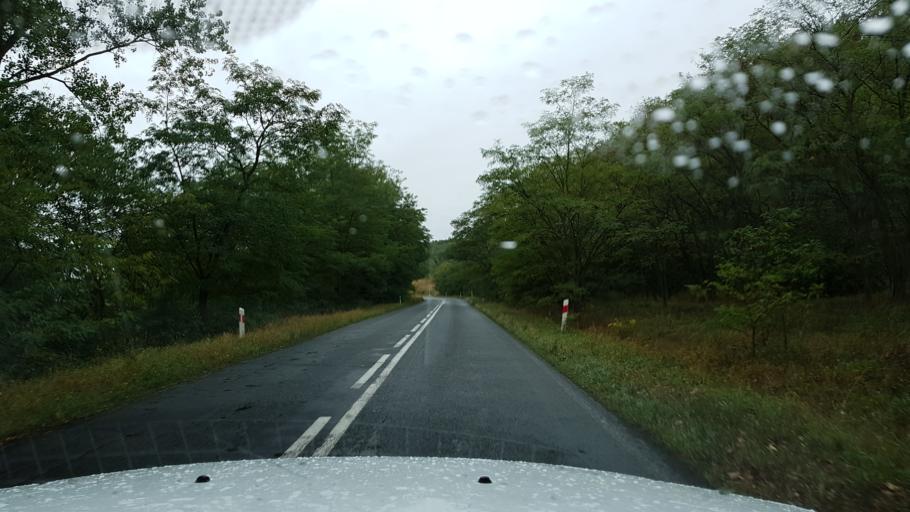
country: PL
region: West Pomeranian Voivodeship
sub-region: Powiat gryfinski
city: Cedynia
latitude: 52.8325
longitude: 14.1674
